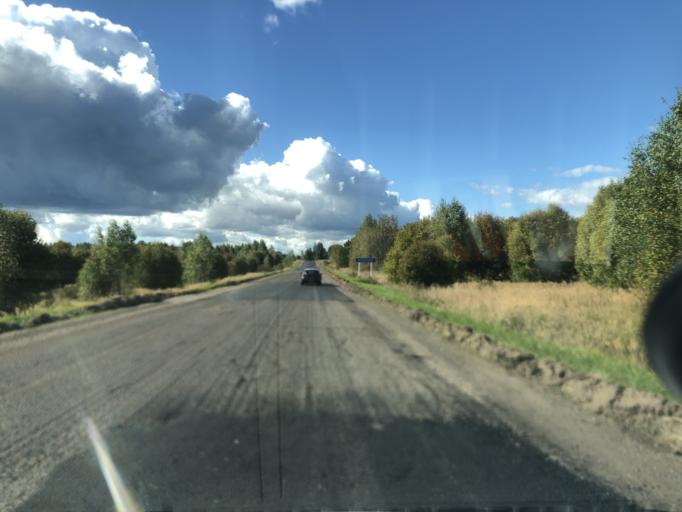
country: RU
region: Jaroslavl
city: Petrovsk
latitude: 56.9606
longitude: 39.3740
